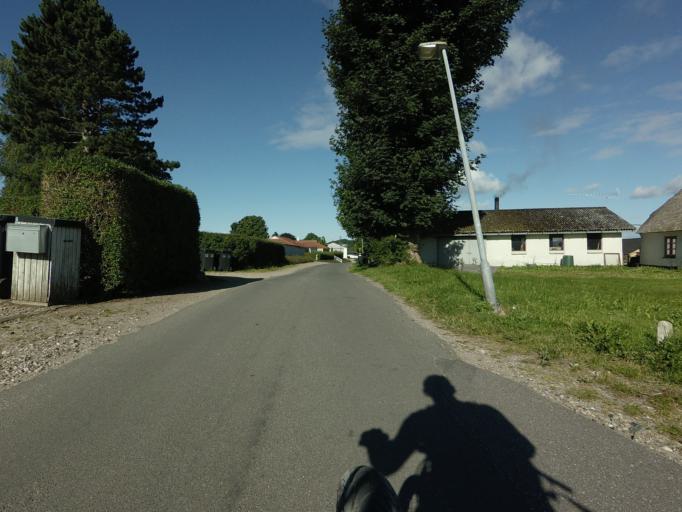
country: DK
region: Central Jutland
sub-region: Horsens Kommune
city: Horsens
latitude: 55.8960
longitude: 9.7714
